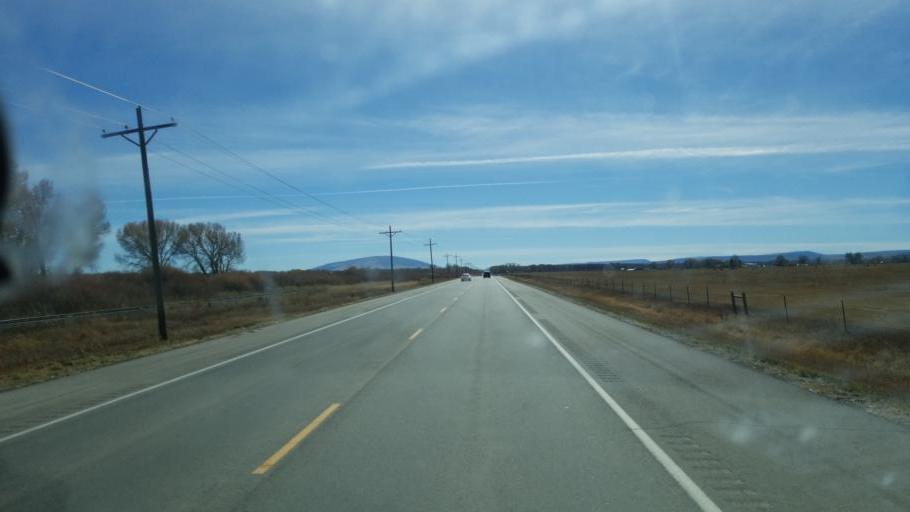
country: US
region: Colorado
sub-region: Conejos County
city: Conejos
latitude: 37.1213
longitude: -106.0018
